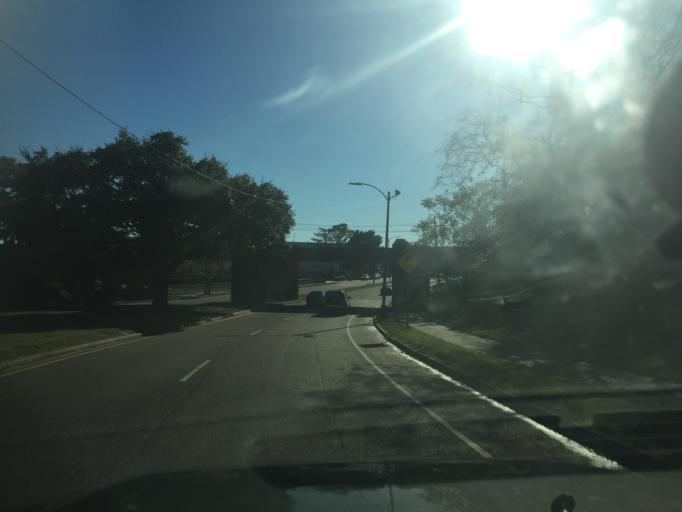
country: US
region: Louisiana
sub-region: Orleans Parish
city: New Orleans
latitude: 29.9892
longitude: -90.0668
